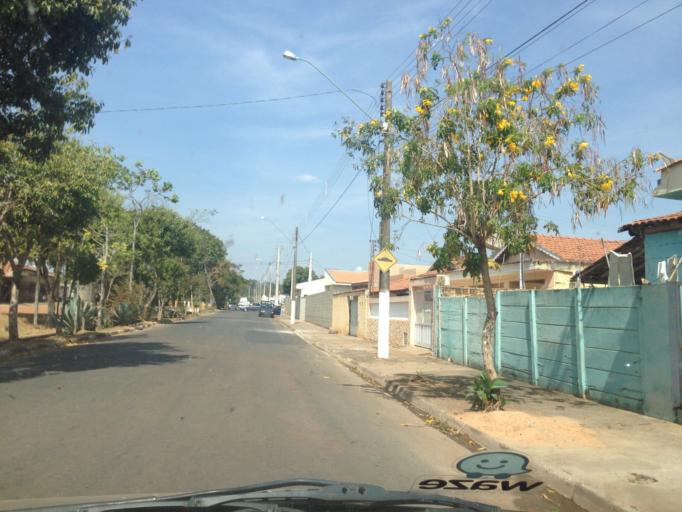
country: BR
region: Sao Paulo
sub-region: Casa Branca
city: Casa Branca
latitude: -21.7742
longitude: -47.0910
